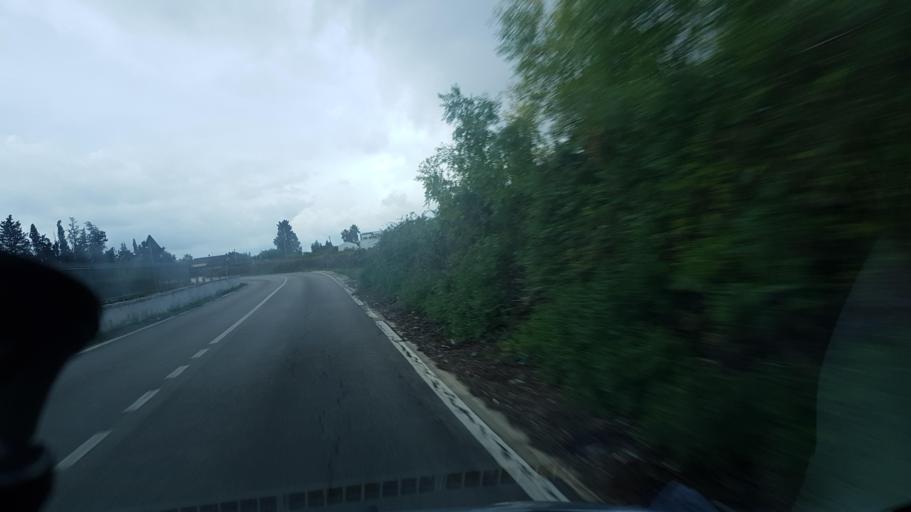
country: IT
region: Apulia
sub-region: Provincia di Lecce
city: Magliano
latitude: 40.3565
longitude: 18.0585
